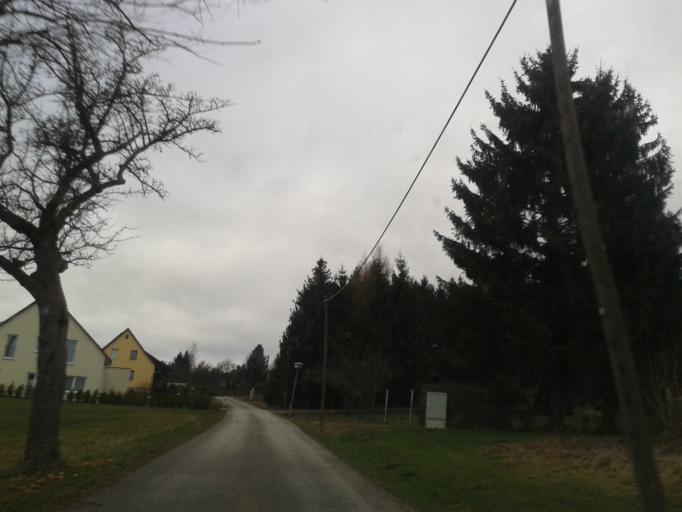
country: DE
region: Saxony
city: Leutersdorf
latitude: 50.9529
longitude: 14.6376
